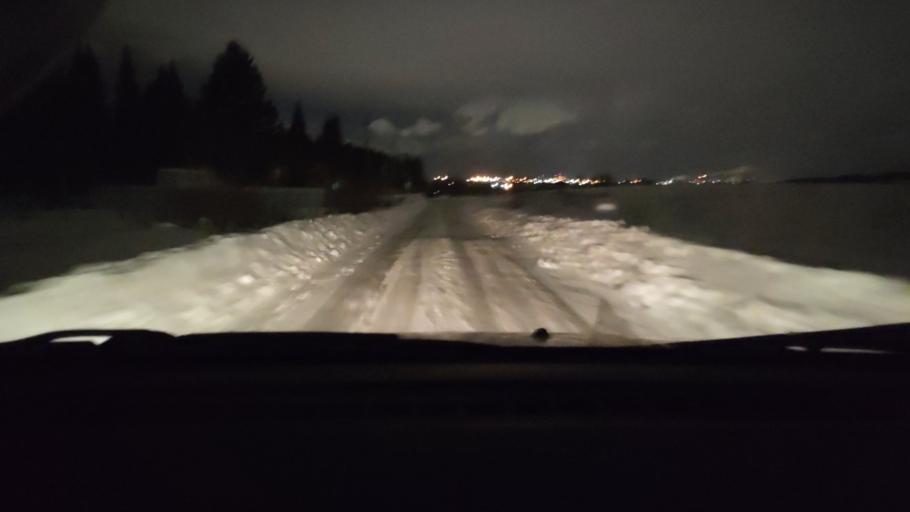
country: RU
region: Perm
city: Froly
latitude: 57.9386
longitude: 56.2604
